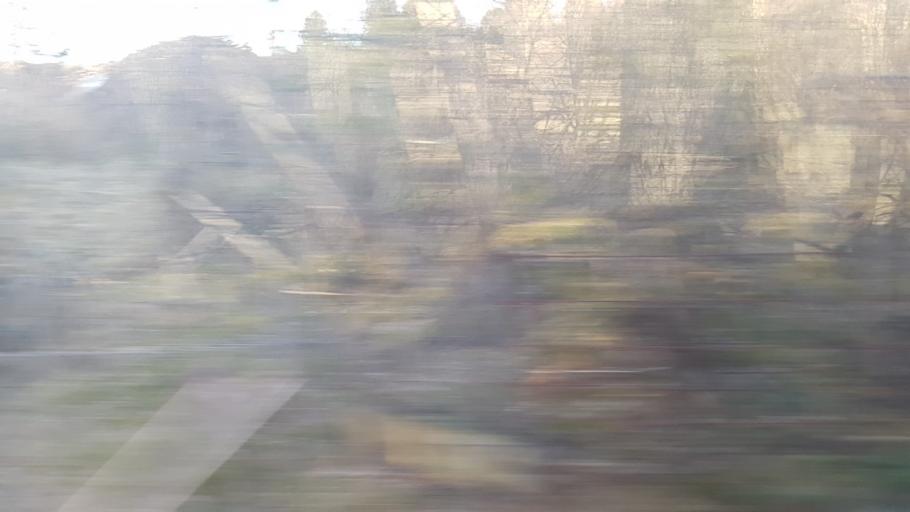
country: NO
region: Sor-Trondelag
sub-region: Malvik
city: Malvik
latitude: 63.4346
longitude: 10.6240
